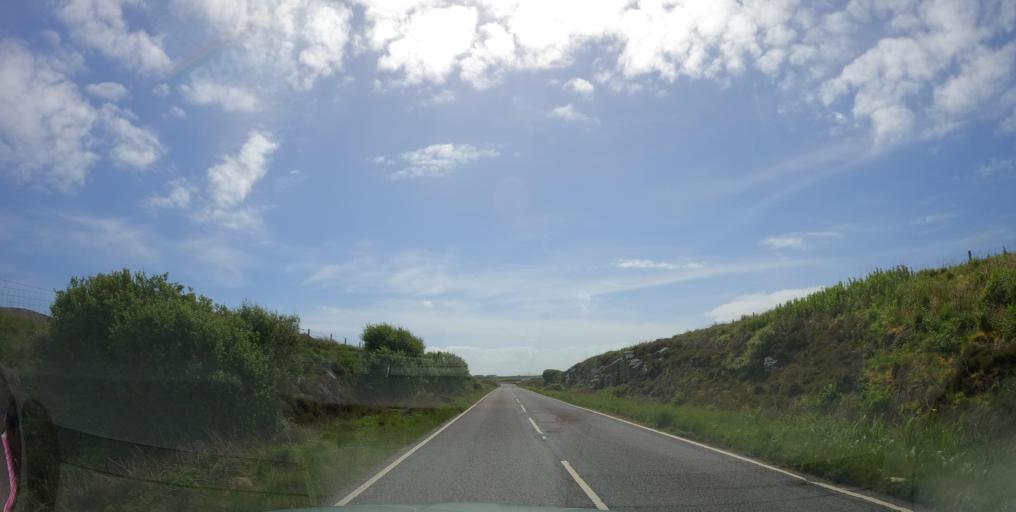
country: GB
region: Scotland
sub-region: Eilean Siar
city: Isle of South Uist
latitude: 57.1923
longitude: -7.3888
